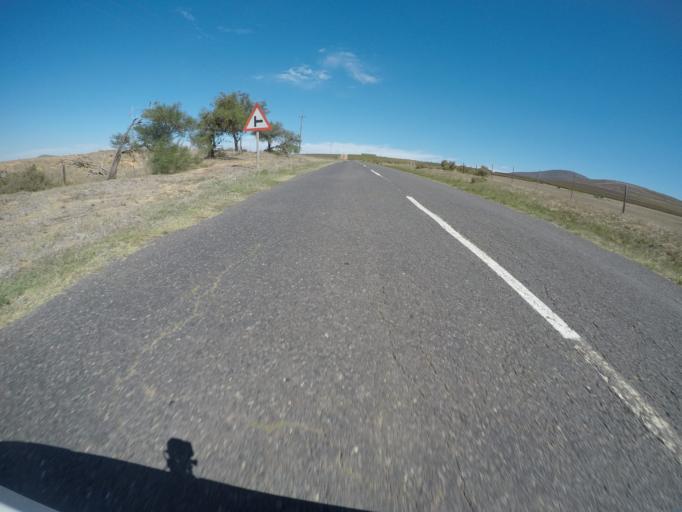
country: ZA
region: Western Cape
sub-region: City of Cape Town
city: Sunset Beach
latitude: -33.7082
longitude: 18.5844
